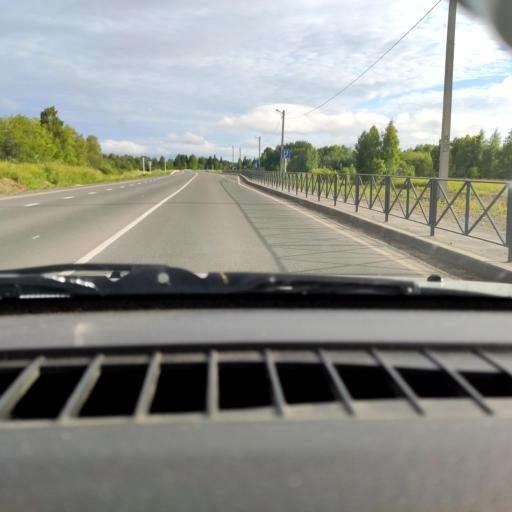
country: RU
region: Perm
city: Kungur
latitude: 57.3496
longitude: 56.9677
